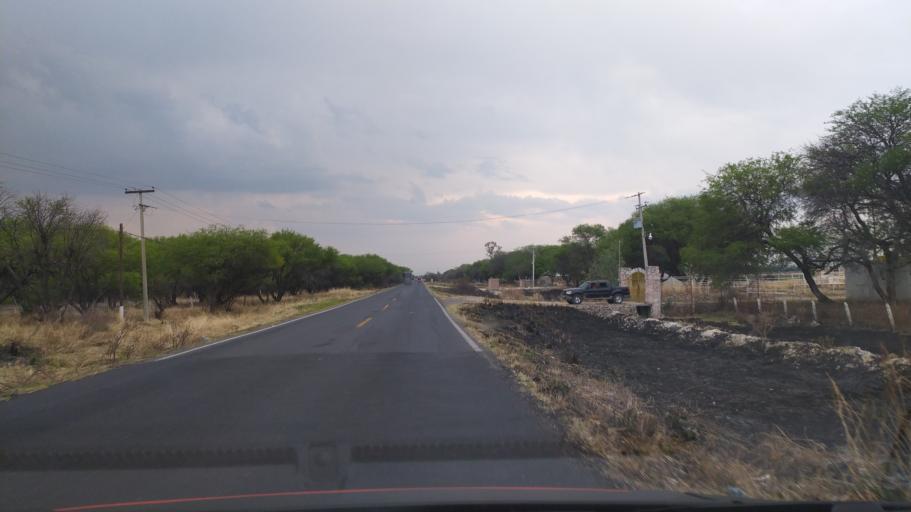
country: MX
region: Guanajuato
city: Ciudad Manuel Doblado
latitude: 20.7660
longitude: -101.9145
